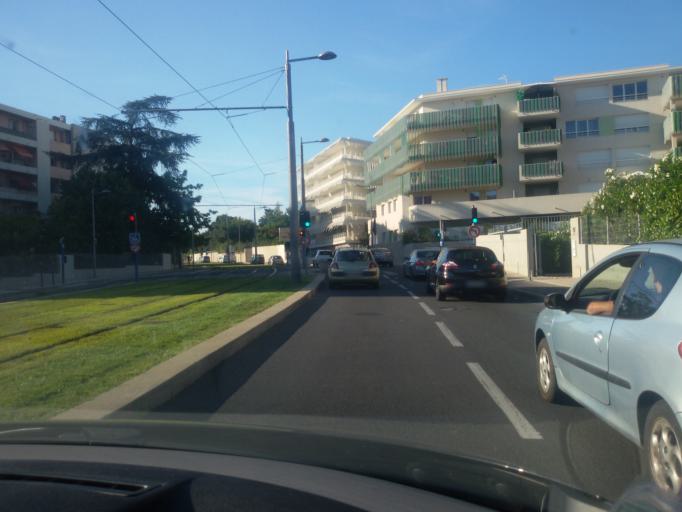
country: FR
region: Languedoc-Roussillon
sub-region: Departement de l'Herault
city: Montpellier
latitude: 43.5938
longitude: 3.8794
